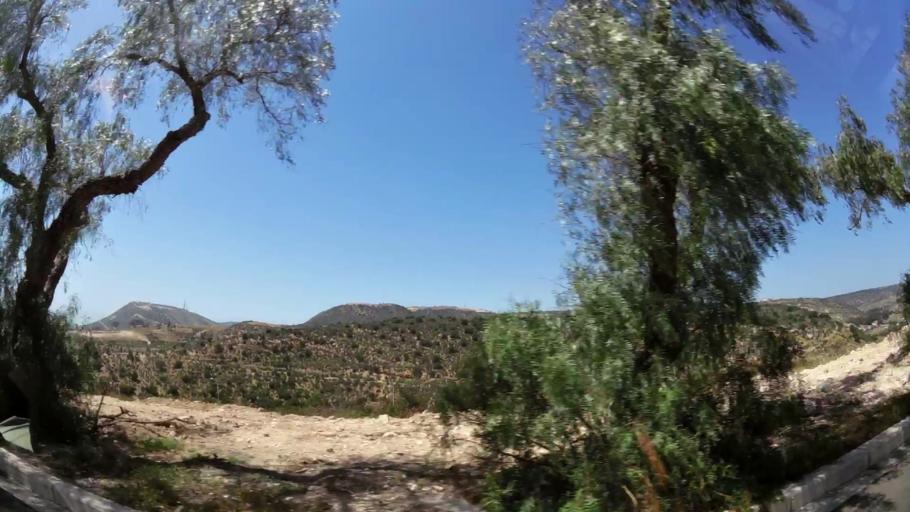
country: MA
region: Souss-Massa-Draa
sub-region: Agadir-Ida-ou-Tnan
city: Agadir
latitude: 30.4304
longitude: -9.6003
